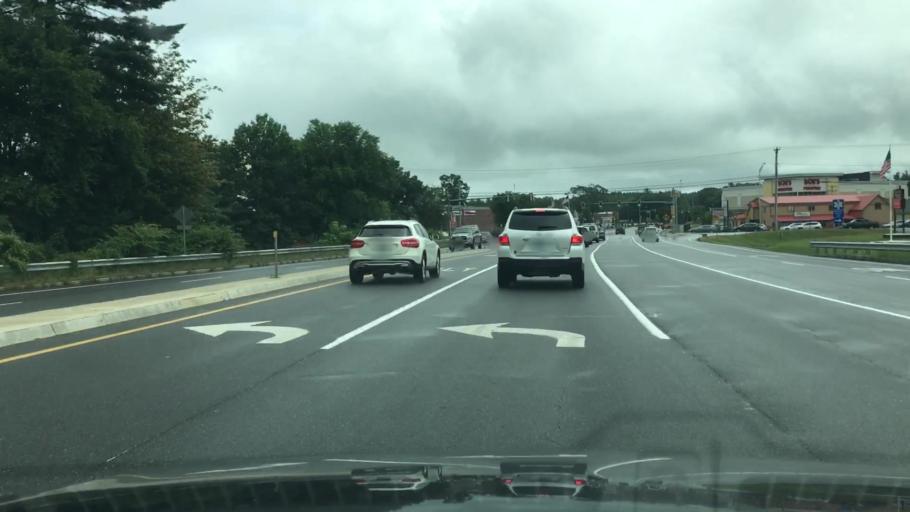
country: US
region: New Hampshire
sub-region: Rockingham County
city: Seabrook
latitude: 42.8938
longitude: -70.8745
